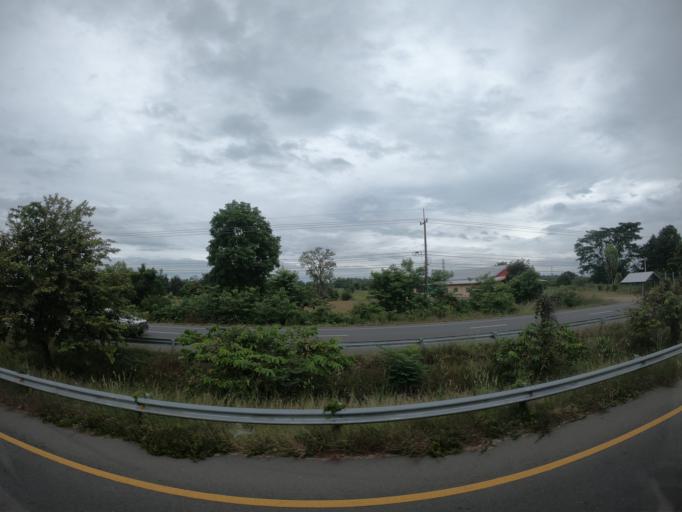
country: TH
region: Roi Et
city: Changhan
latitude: 16.1145
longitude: 103.4977
